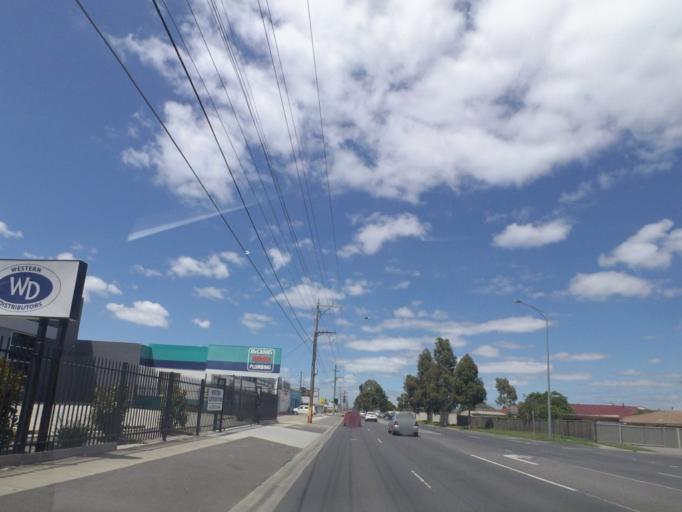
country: AU
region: Victoria
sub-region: Brimbank
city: Albion
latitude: -37.7537
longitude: 144.8331
